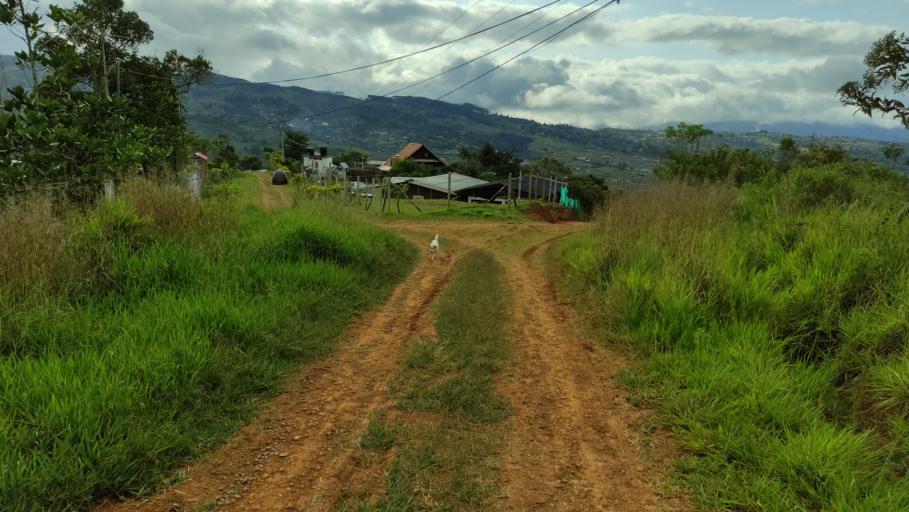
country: CO
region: Valle del Cauca
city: Dagua
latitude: 3.5370
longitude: -76.6395
